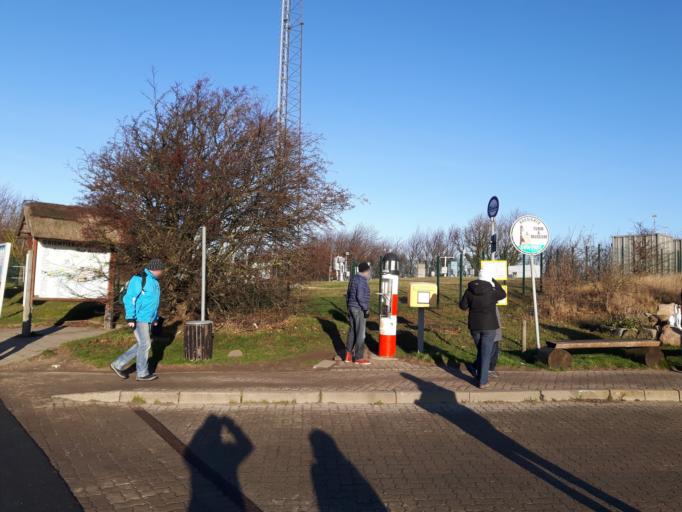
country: DE
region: Mecklenburg-Vorpommern
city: Altenkirchen
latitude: 54.6788
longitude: 13.4341
